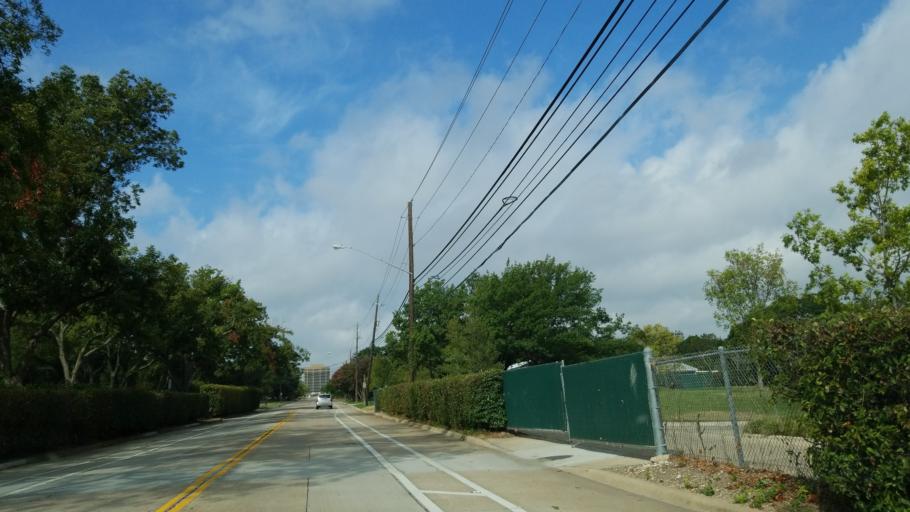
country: US
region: Texas
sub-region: Dallas County
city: Addison
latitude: 32.9332
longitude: -96.7953
